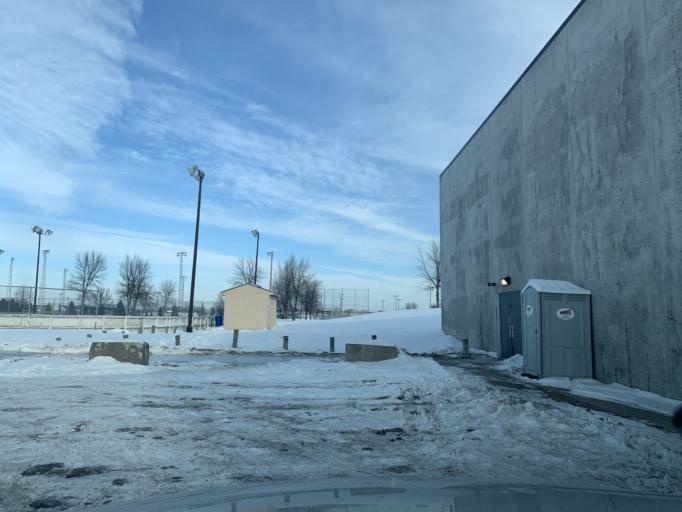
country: US
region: Minnesota
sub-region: Wright County
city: Buffalo
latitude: 45.1615
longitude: -93.8491
